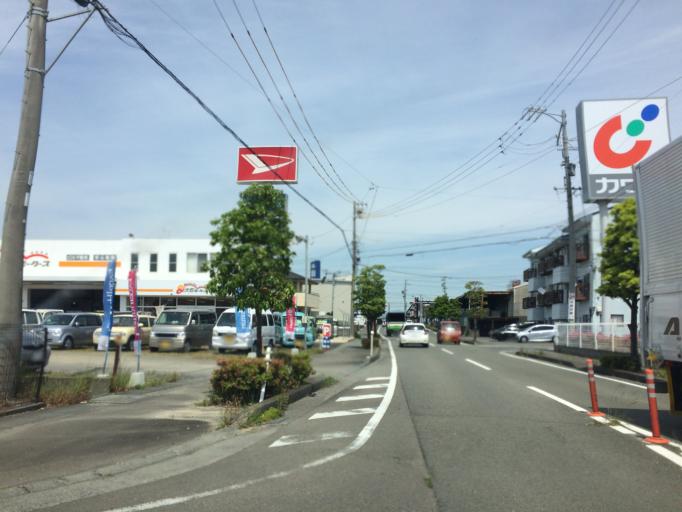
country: JP
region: Shizuoka
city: Shimada
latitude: 34.7611
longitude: 138.2478
